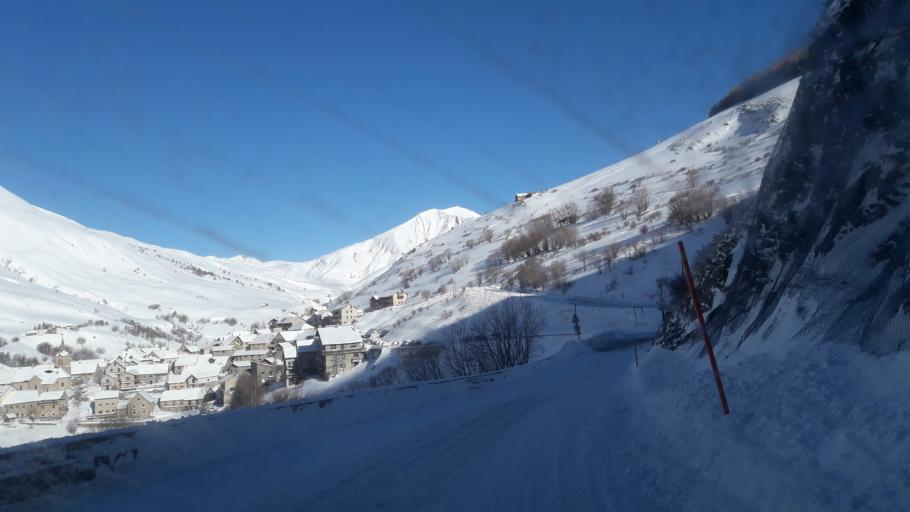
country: FR
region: Rhone-Alpes
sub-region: Departement de l'Isere
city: Mont-de-Lans
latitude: 45.0513
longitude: 6.2889
